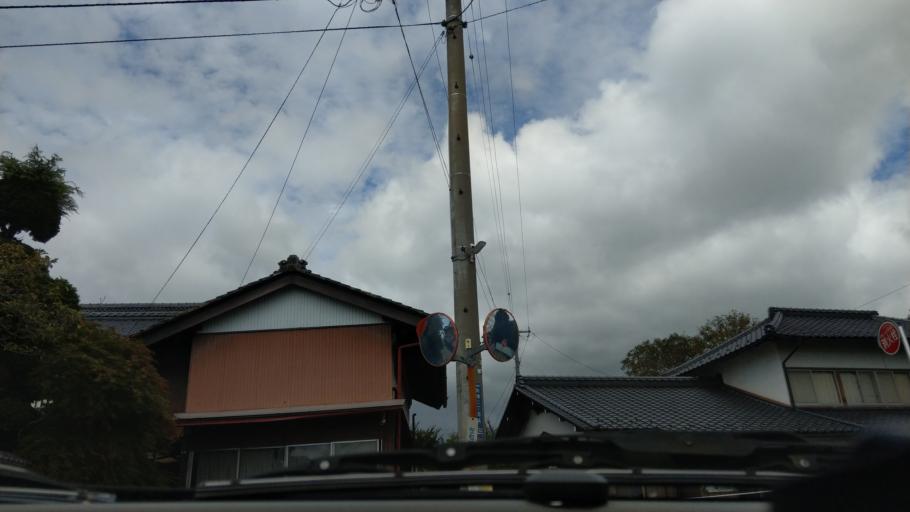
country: JP
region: Nagano
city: Komoro
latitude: 36.3214
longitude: 138.4353
